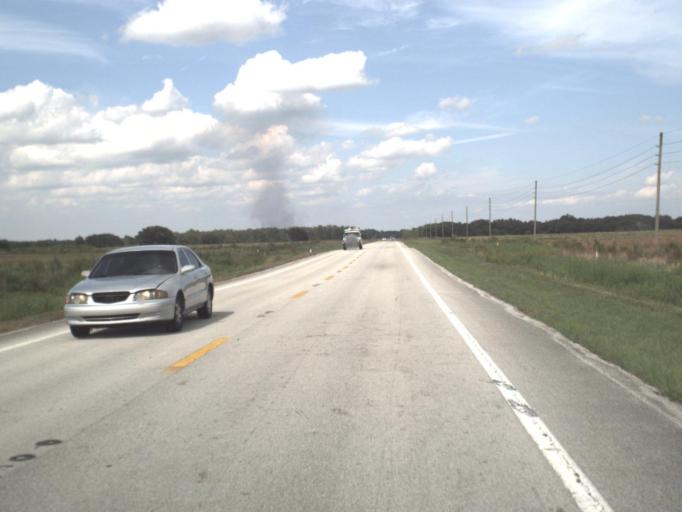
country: US
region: Florida
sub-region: Okeechobee County
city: Cypress Quarters
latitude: 27.4777
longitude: -80.8074
